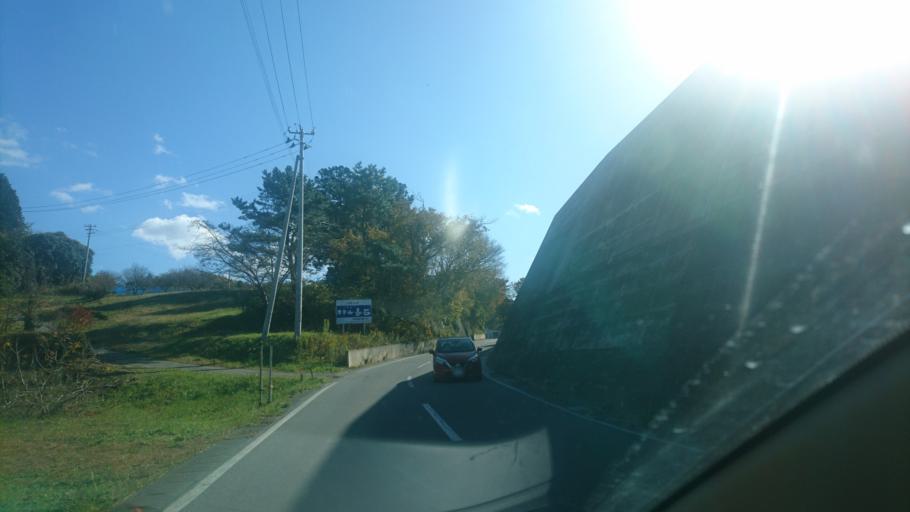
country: JP
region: Iwate
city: Ofunato
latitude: 38.9977
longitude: 141.7207
